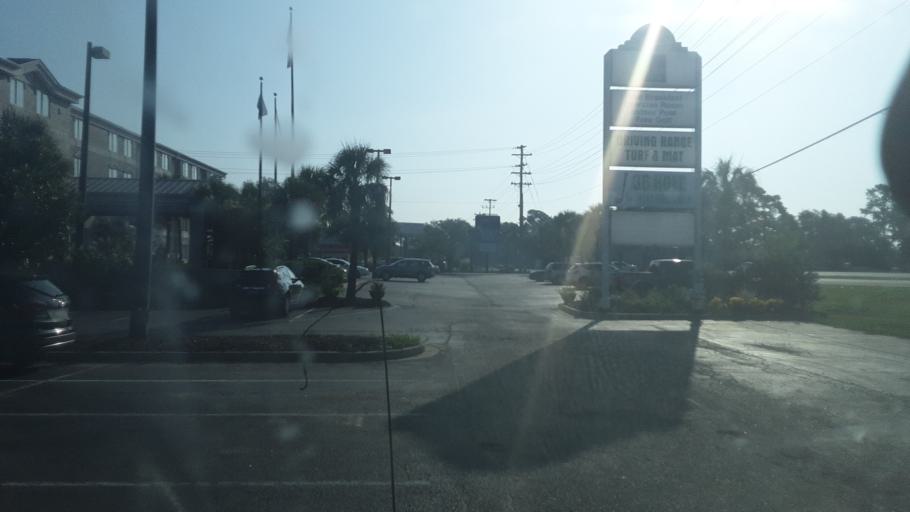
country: US
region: South Carolina
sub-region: Horry County
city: Little River
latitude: 33.8689
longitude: -78.6325
